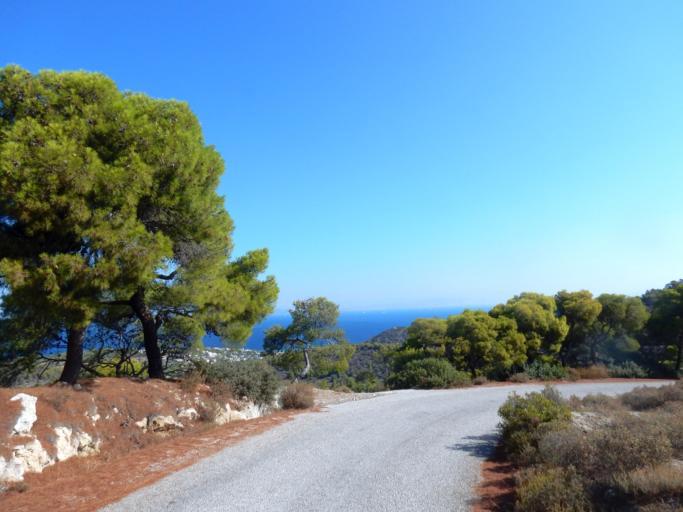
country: GR
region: Attica
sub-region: Nomos Piraios
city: Vathi
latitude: 37.7545
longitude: 23.5360
